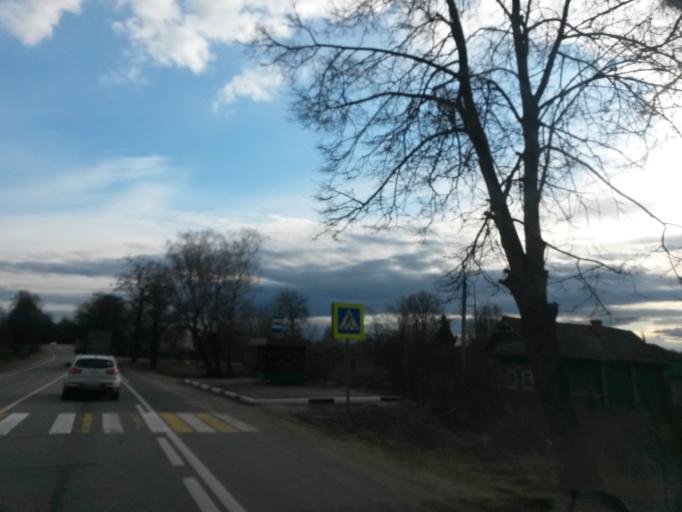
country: RU
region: Vladimir
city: Strunino
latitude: 56.5722
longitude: 38.5936
